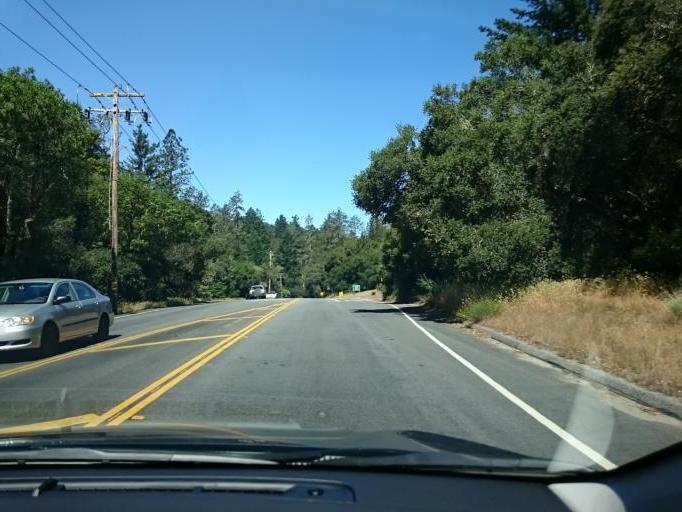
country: US
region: California
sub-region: Santa Cruz County
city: Mount Hermon
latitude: 37.0422
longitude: -122.0483
